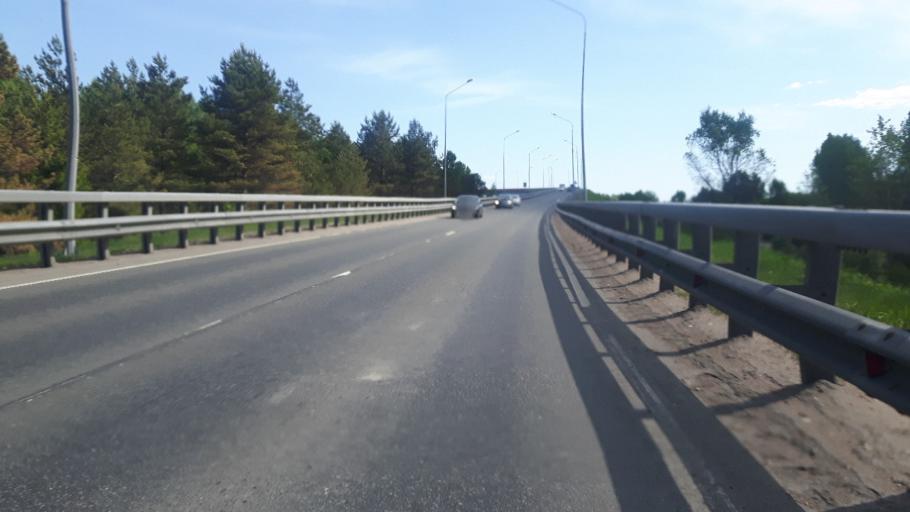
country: RU
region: Leningrad
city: Vyborg
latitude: 60.7420
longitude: 28.6820
